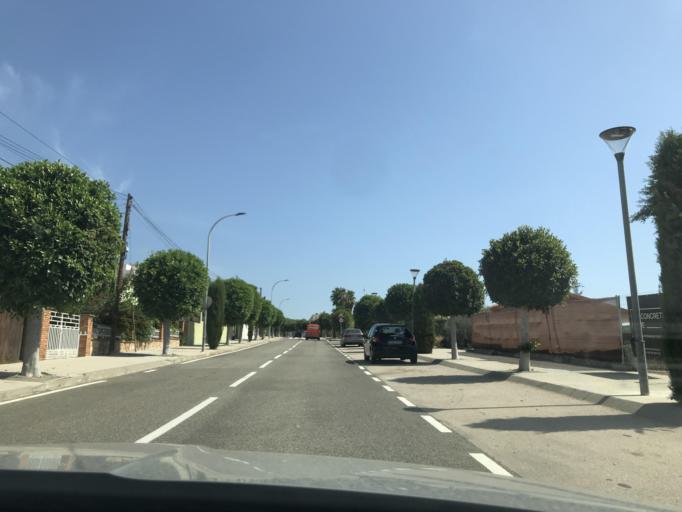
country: ES
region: Catalonia
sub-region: Provincia de Tarragona
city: Altafulla
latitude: 41.1840
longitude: 1.3775
